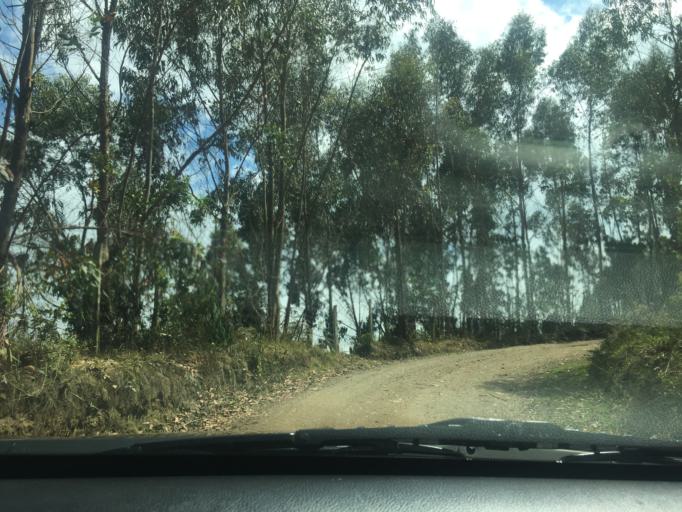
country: CO
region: Cundinamarca
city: Facatativa
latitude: 4.7928
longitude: -74.3767
